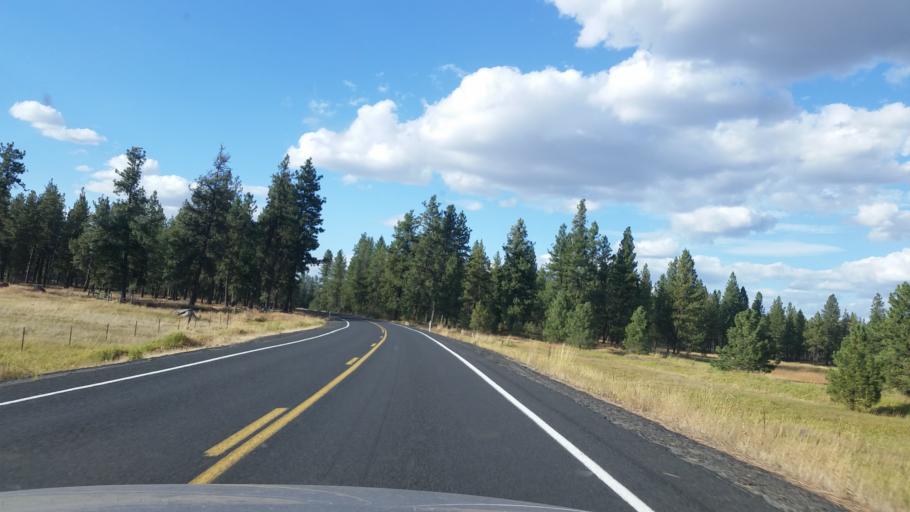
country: US
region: Washington
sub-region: Spokane County
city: Cheney
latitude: 47.4258
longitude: -117.5654
